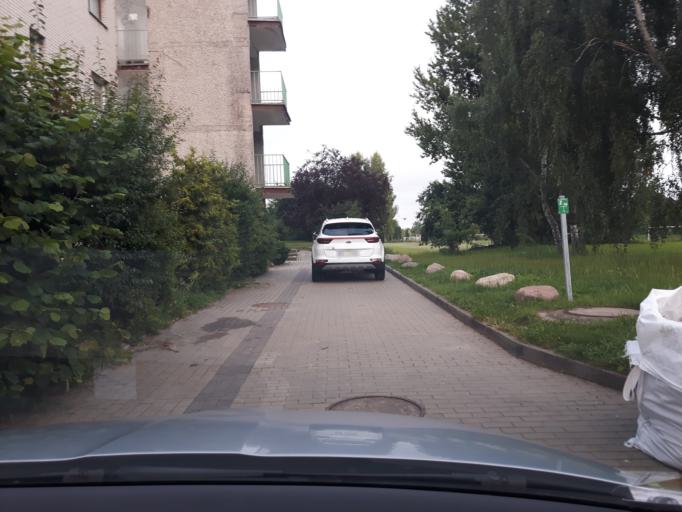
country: PL
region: Pomeranian Voivodeship
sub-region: Sopot
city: Sopot
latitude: 54.4318
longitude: 18.5810
